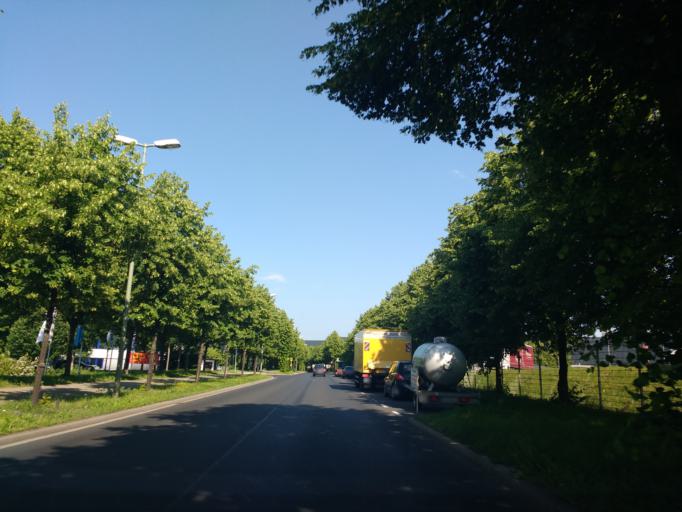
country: DE
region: Hesse
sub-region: Regierungsbezirk Kassel
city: Lohfelden
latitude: 51.2743
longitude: 9.5160
